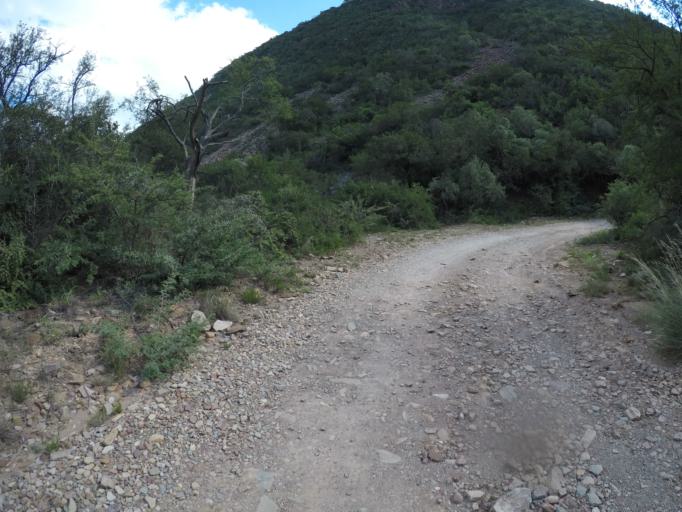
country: ZA
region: Eastern Cape
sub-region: Cacadu District Municipality
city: Kareedouw
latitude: -33.6504
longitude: 24.3358
